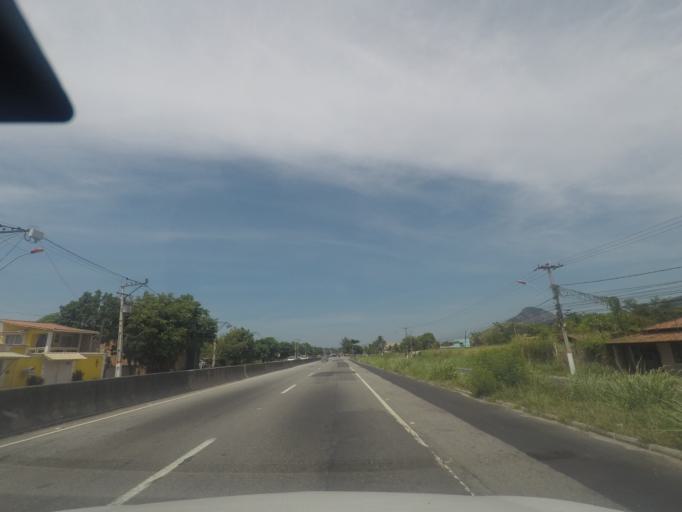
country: BR
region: Rio de Janeiro
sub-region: Marica
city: Marica
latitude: -22.9238
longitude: -42.8619
